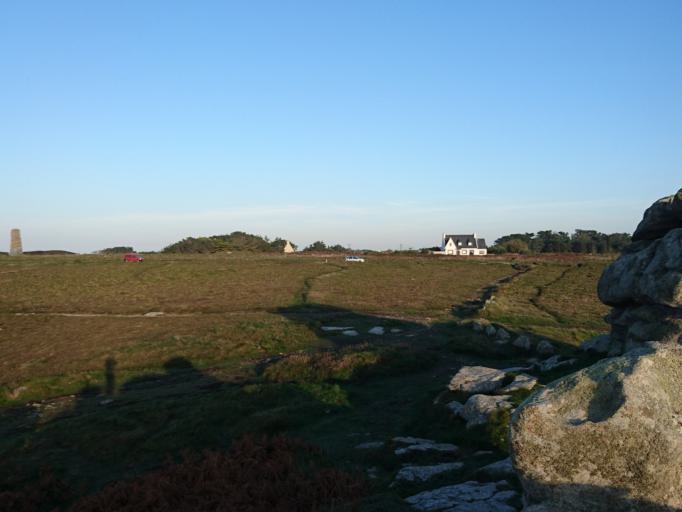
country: FR
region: Brittany
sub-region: Departement du Finistere
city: Landunvez
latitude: 48.5402
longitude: -4.7502
